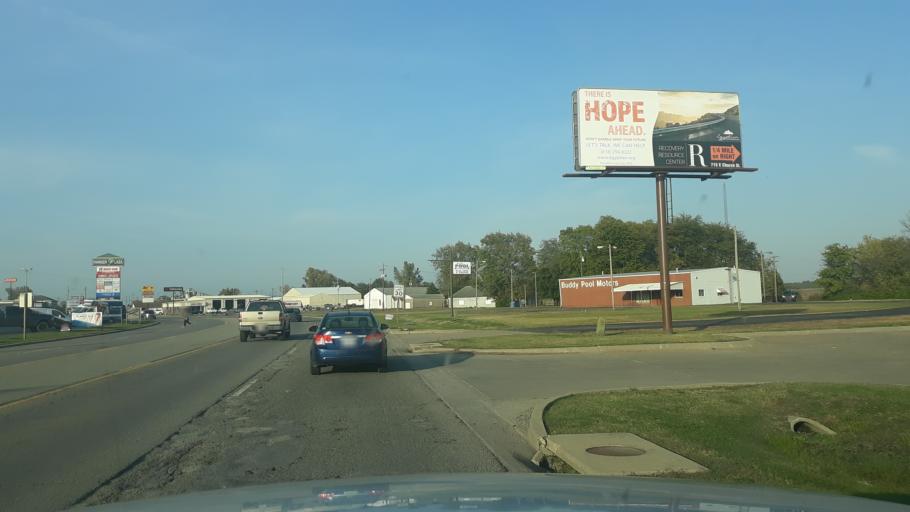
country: US
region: Illinois
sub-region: Saline County
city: Harrisburg
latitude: 37.7336
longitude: -88.5338
